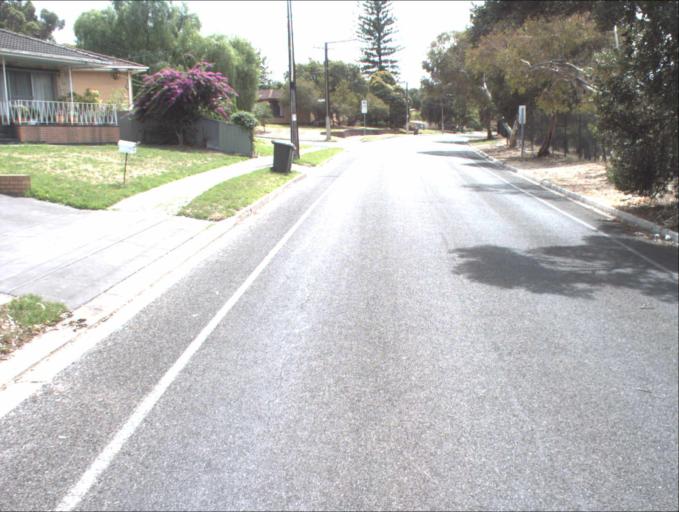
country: AU
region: South Australia
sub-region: Campbelltown
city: Paradise
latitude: -34.8615
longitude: 138.6674
